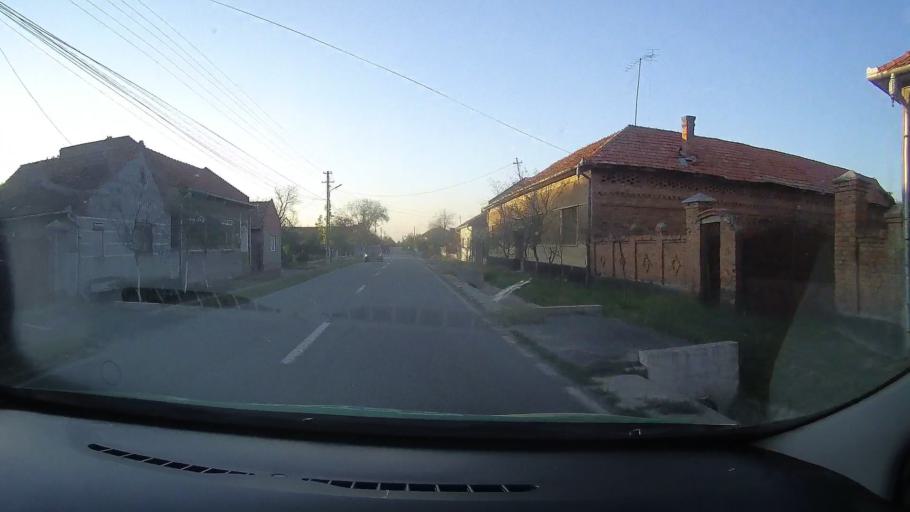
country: RO
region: Timis
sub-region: Comuna Traian Vuia
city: Traian Vuia
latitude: 45.7946
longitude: 22.0696
